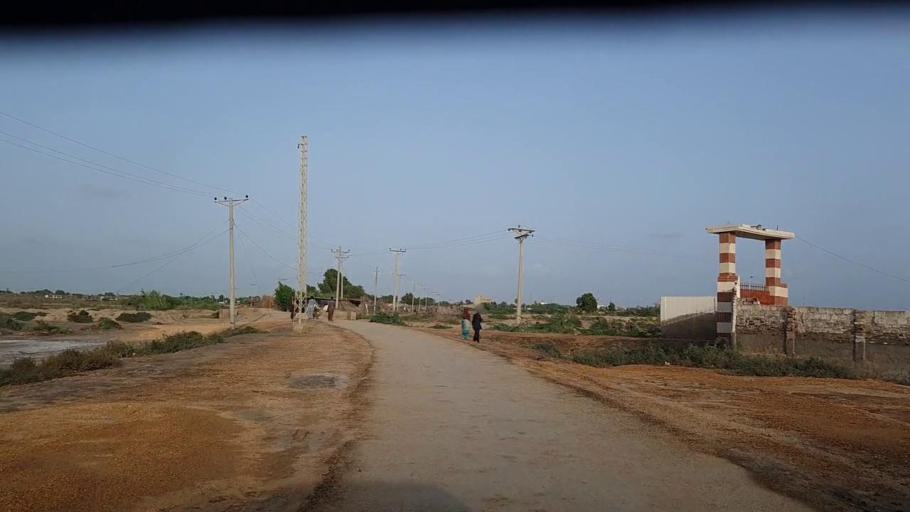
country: PK
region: Sindh
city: Thatta
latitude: 24.7604
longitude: 67.9068
